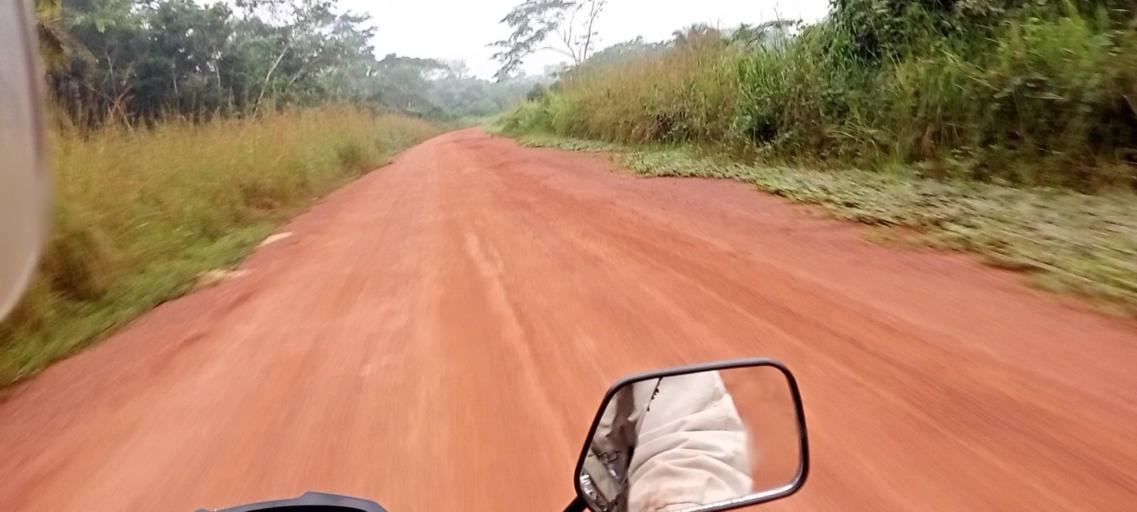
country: CD
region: Eastern Province
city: Kisangani
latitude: -0.0793
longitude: 25.5985
